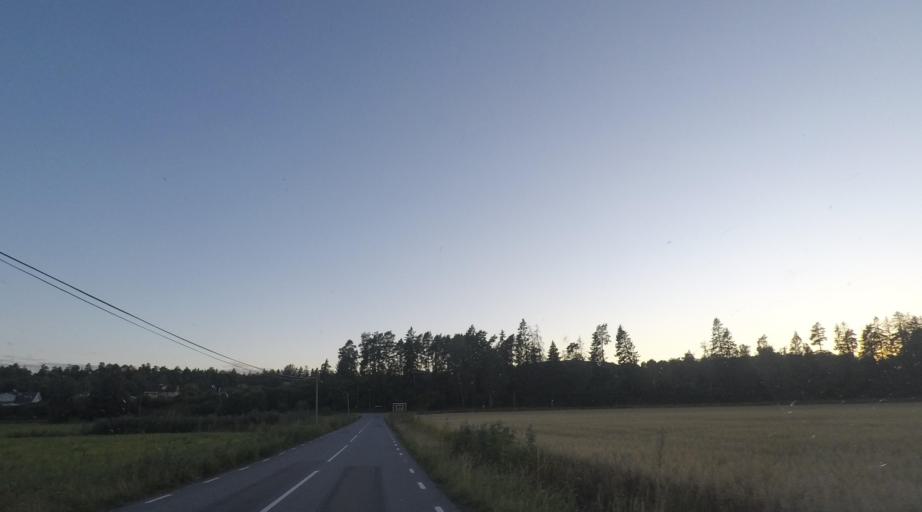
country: SE
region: Soedermanland
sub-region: Trosa Kommun
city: Trosa
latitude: 58.9689
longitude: 17.6970
